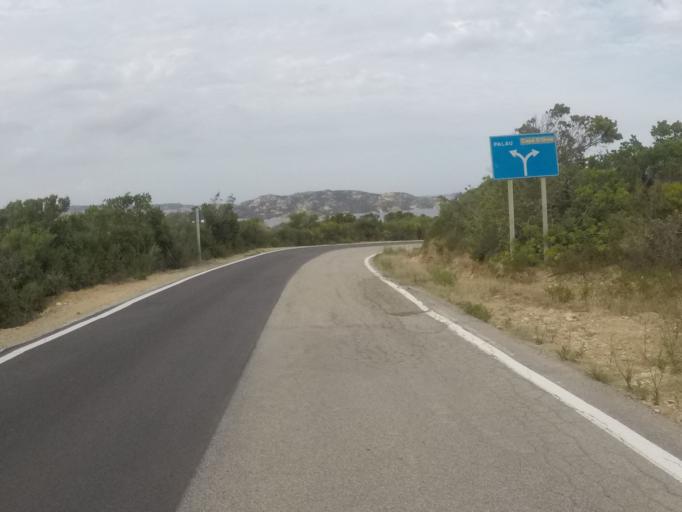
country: IT
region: Sardinia
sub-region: Provincia di Olbia-Tempio
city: Palau
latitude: 41.1709
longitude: 9.4025
